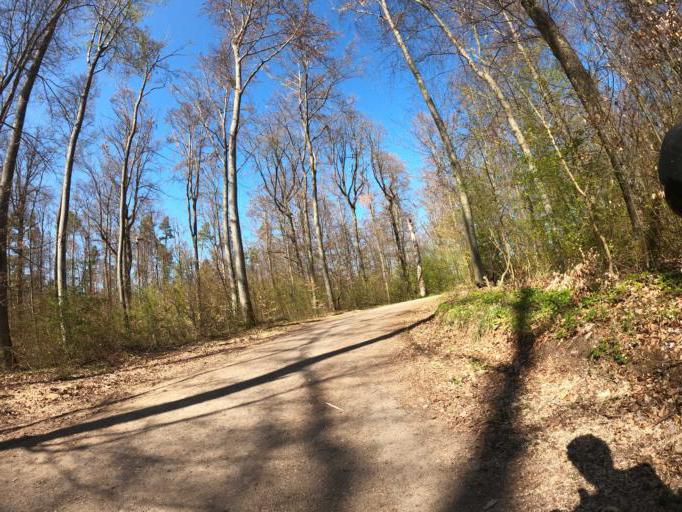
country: DE
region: Baden-Wuerttemberg
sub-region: Karlsruhe Region
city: Wiernsheim
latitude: 48.8959
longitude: 8.8274
